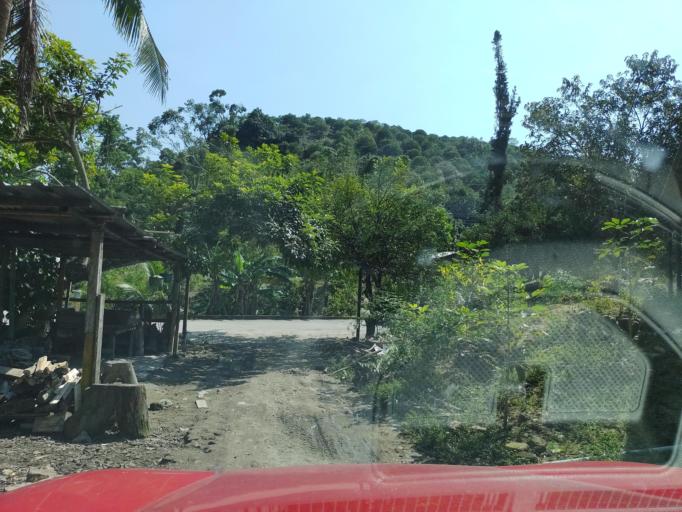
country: MX
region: Veracruz
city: Agua Dulce
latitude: 20.3375
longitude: -97.2005
